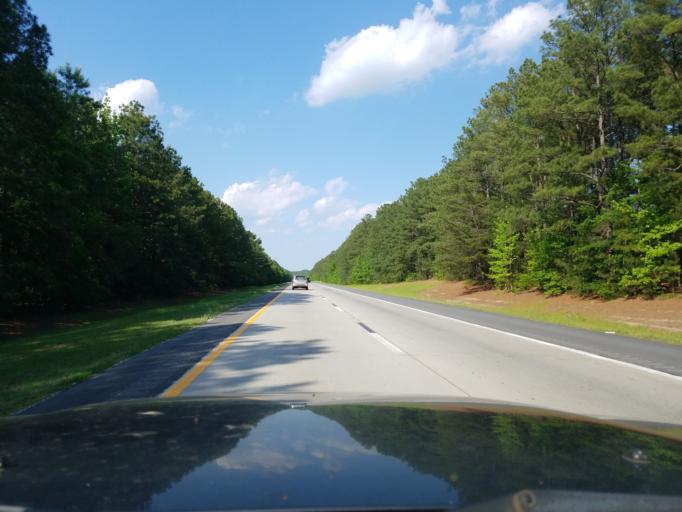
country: US
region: North Carolina
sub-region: Granville County
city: Creedmoor
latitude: 36.1754
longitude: -78.7020
